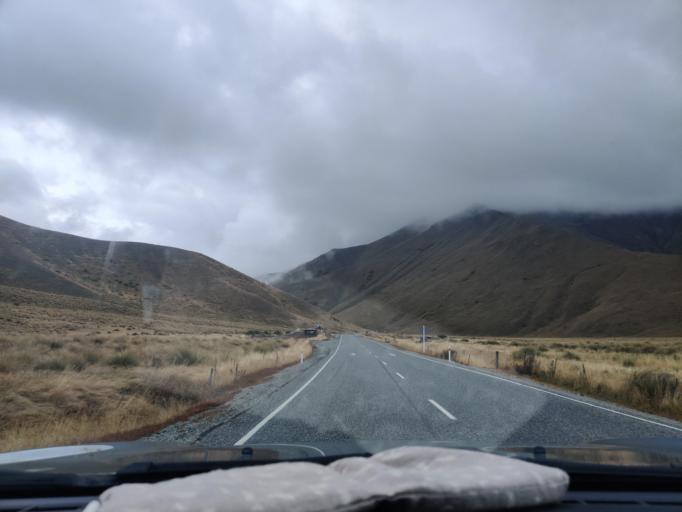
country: NZ
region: Otago
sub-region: Queenstown-Lakes District
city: Wanaka
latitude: -44.5781
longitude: 169.6280
